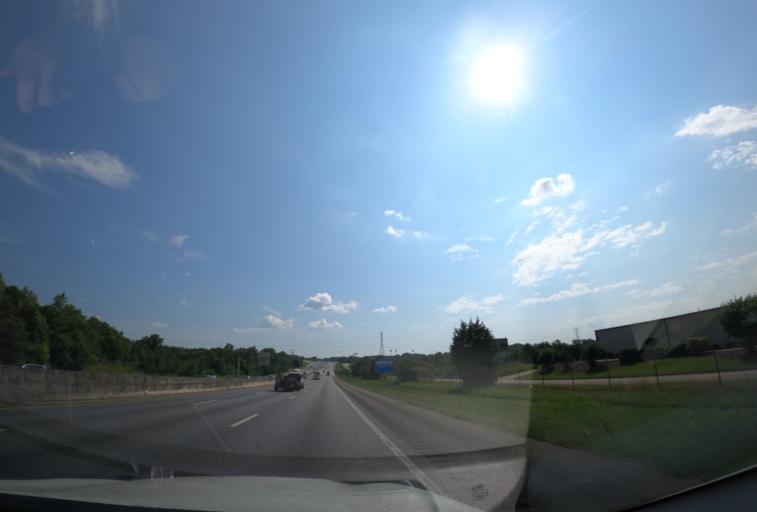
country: US
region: South Carolina
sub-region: Greenville County
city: Gantt
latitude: 34.7811
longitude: -82.4565
